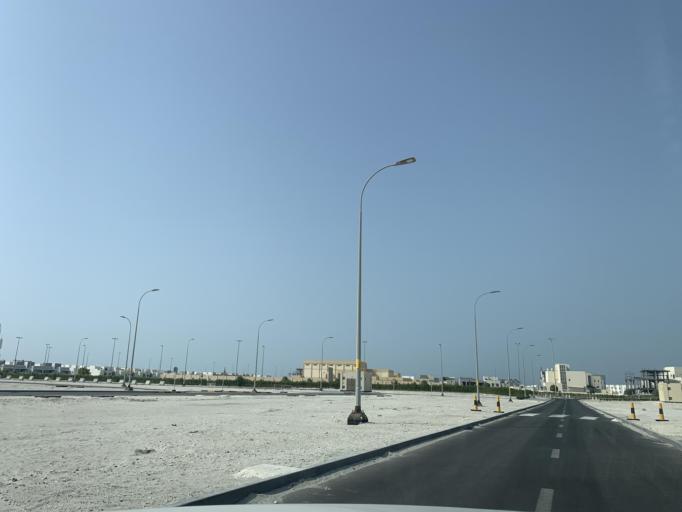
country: BH
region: Muharraq
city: Al Muharraq
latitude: 26.3075
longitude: 50.6323
